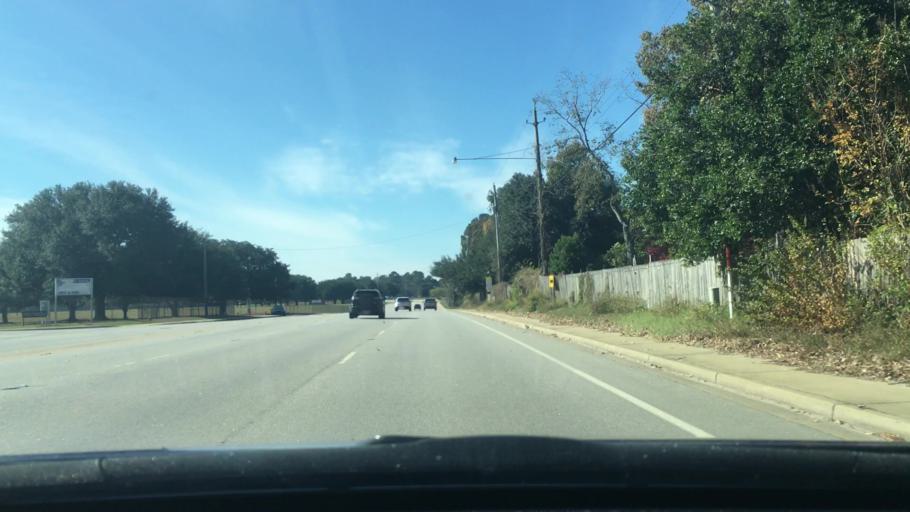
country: US
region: South Carolina
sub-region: Sumter County
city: South Sumter
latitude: 33.9024
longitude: -80.3903
